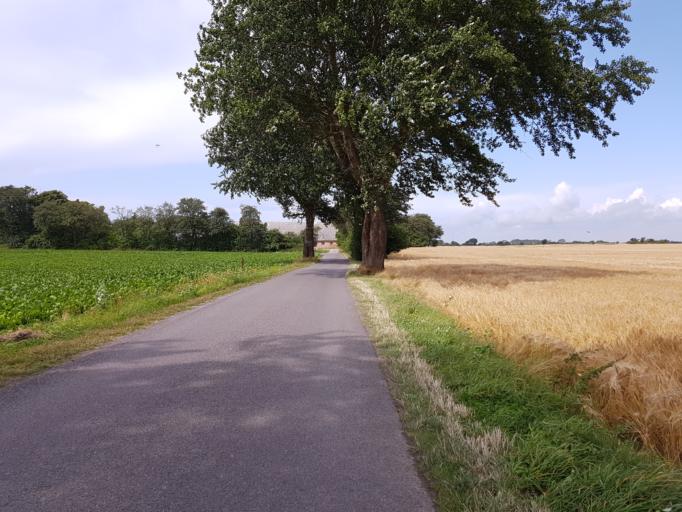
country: DK
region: Zealand
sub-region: Guldborgsund Kommune
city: Nykobing Falster
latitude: 54.5680
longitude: 11.9548
